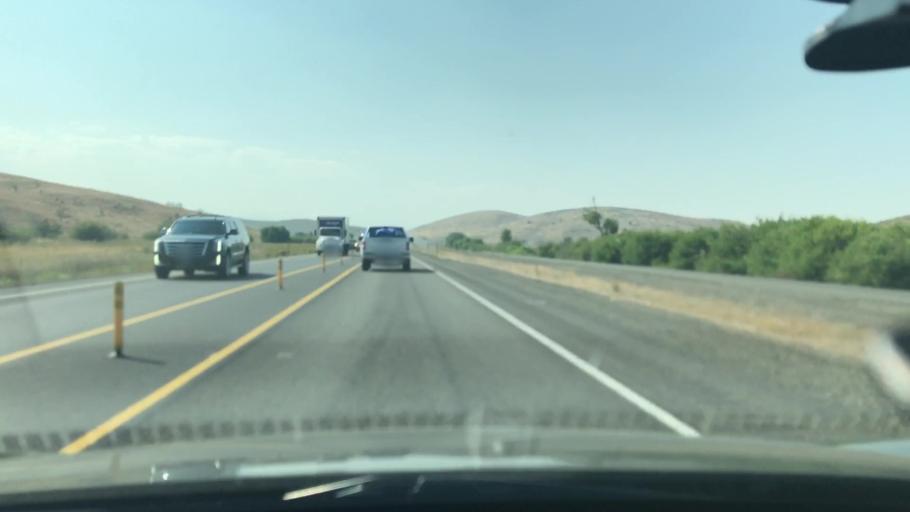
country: US
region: Oregon
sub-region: Baker County
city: Baker City
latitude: 44.6778
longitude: -117.6460
